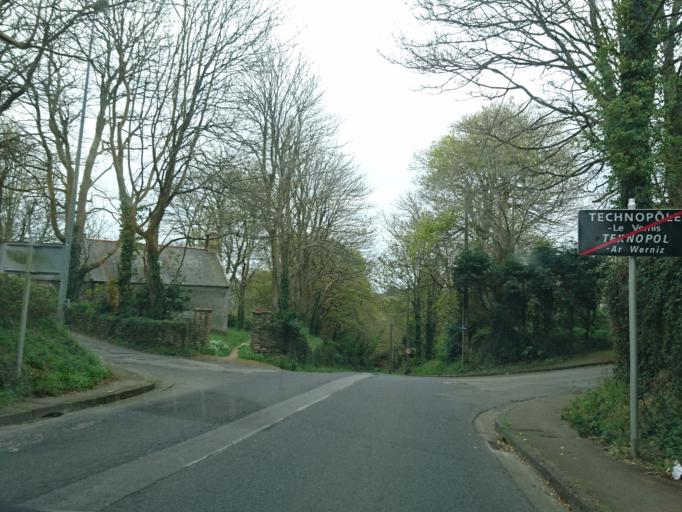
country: FR
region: Brittany
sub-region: Departement du Finistere
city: Roscanvel
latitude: 48.3650
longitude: -4.5489
